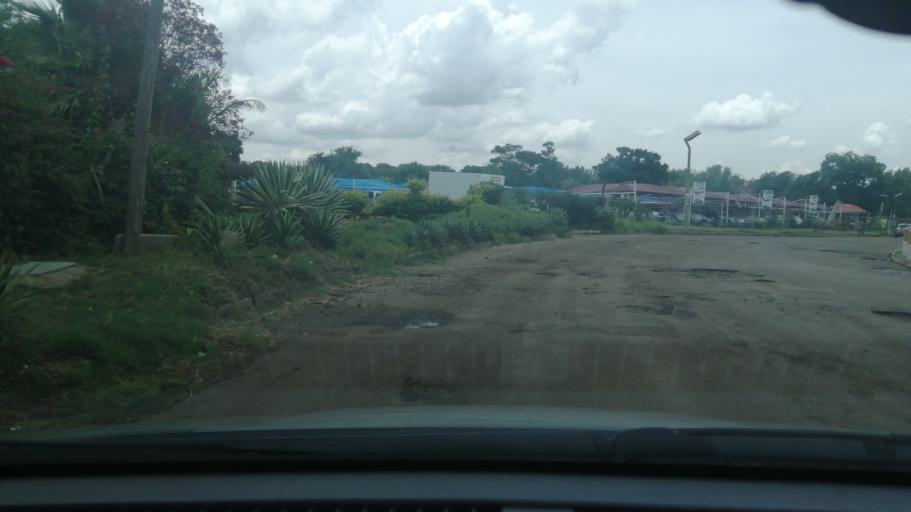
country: ZW
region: Harare
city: Harare
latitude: -17.8019
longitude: 31.0387
